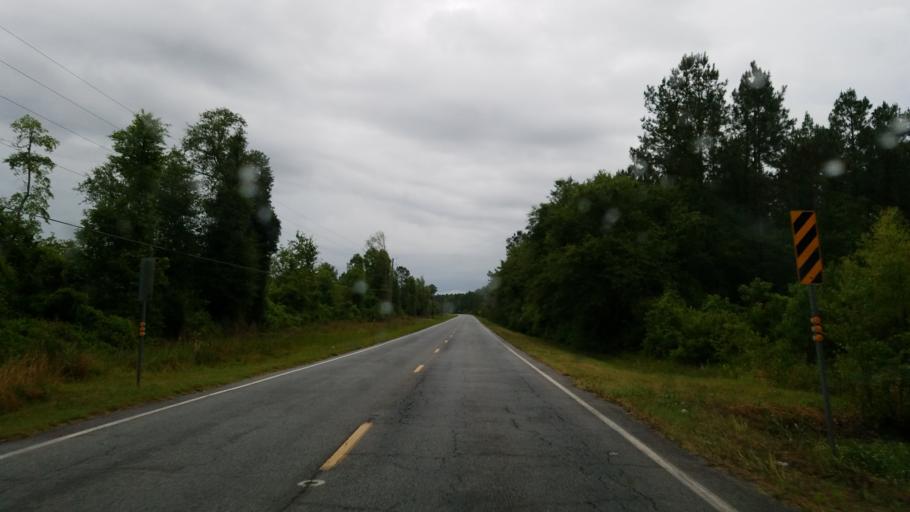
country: US
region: Georgia
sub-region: Berrien County
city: Ray City
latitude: 31.0563
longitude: -83.1467
